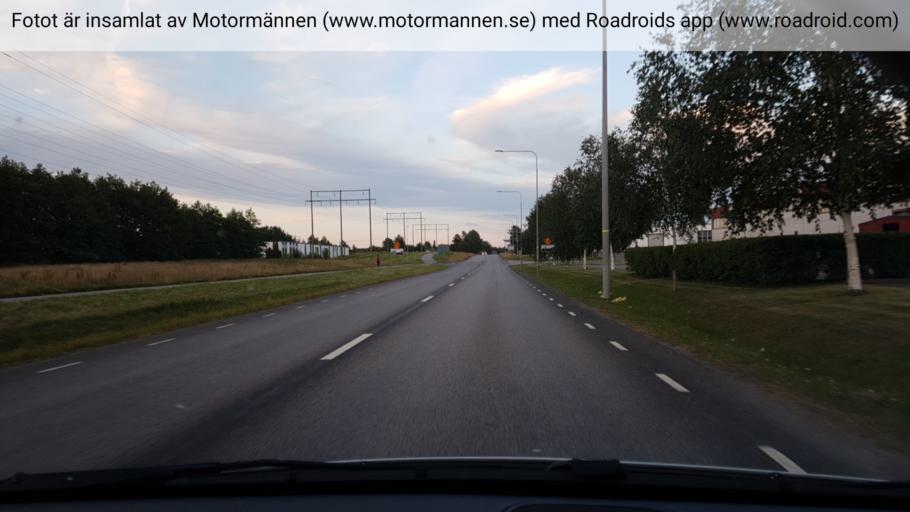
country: SE
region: Vaestra Goetaland
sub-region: Tibro Kommun
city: Tibro
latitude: 58.4134
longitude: 14.1489
